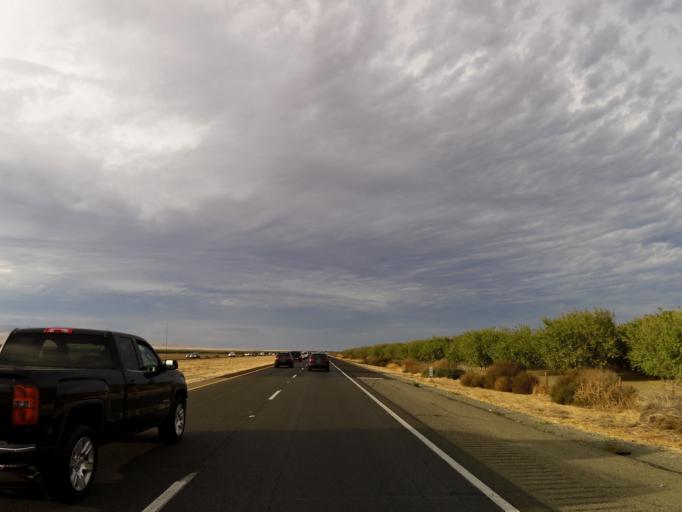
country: US
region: California
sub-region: Fresno County
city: Huron
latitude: 36.1912
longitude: -120.2040
